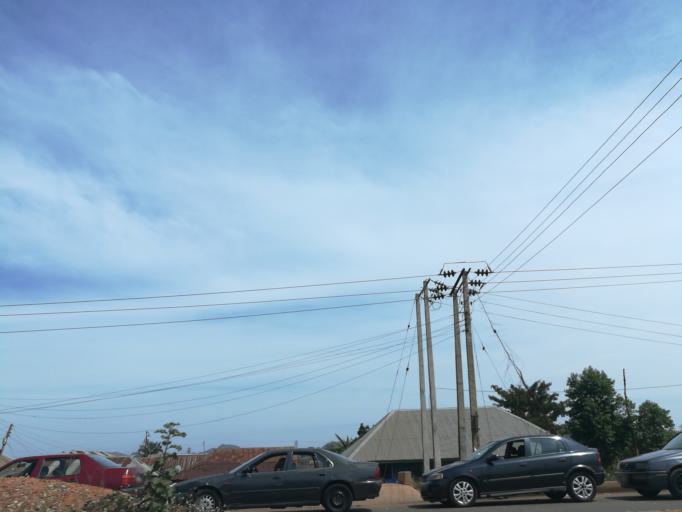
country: NG
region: Plateau
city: Bukuru
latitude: 9.7697
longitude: 8.8603
